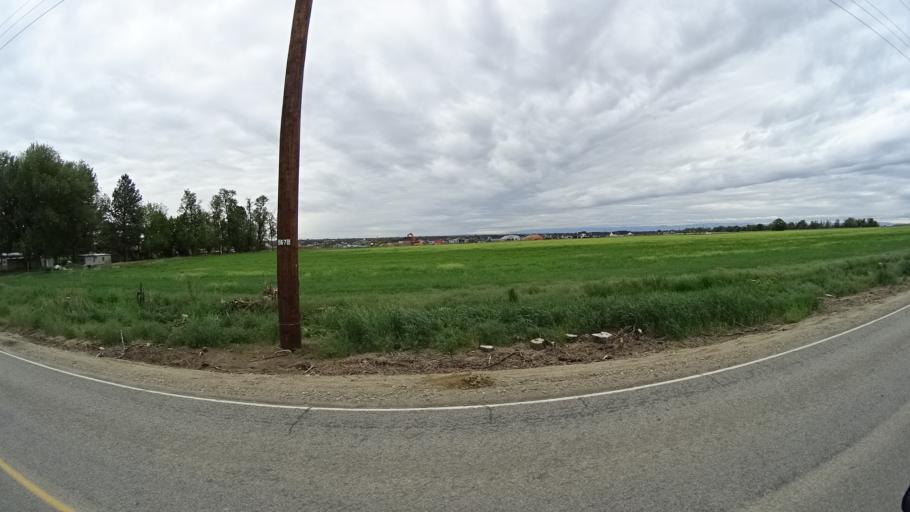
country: US
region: Idaho
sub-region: Ada County
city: Star
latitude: 43.7212
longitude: -116.4248
